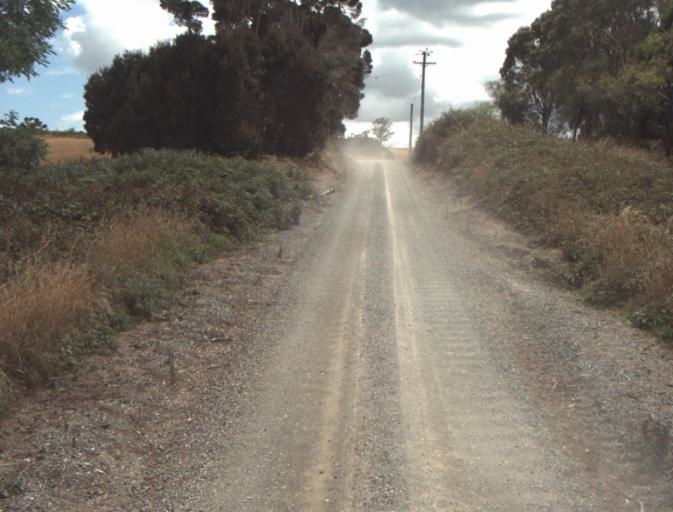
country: AU
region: Tasmania
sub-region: Launceston
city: Mayfield
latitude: -41.1943
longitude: 147.1703
